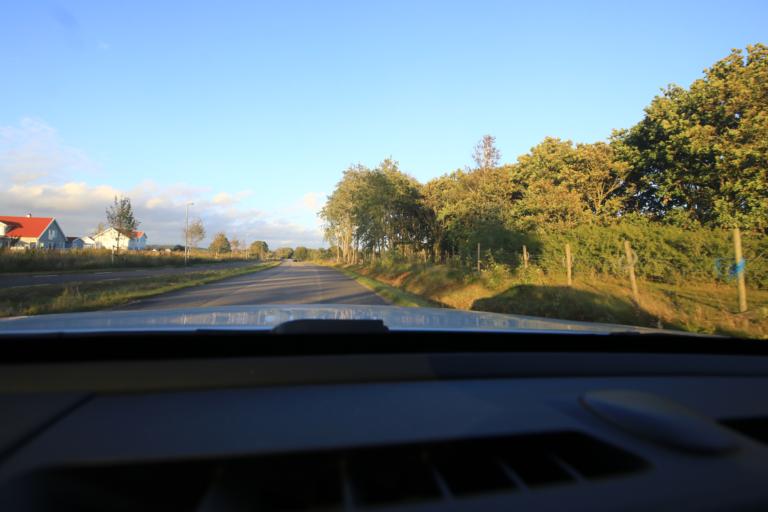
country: SE
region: Halland
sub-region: Varbergs Kommun
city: Varberg
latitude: 57.1429
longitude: 12.2338
